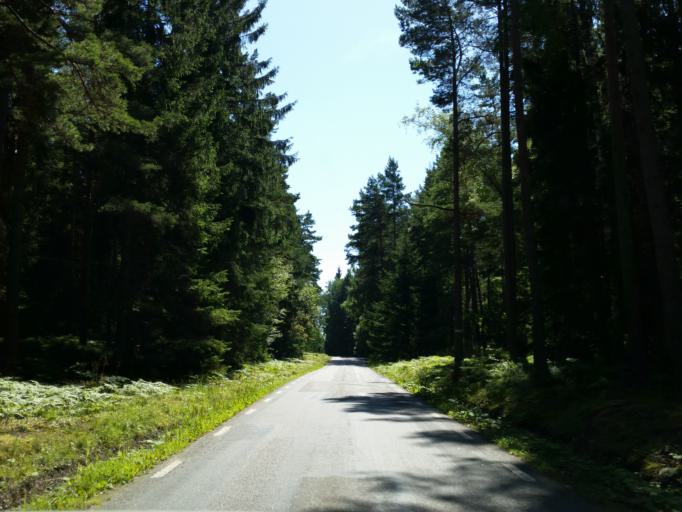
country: SE
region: Soedermanland
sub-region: Trosa Kommun
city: Trosa
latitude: 58.9663
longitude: 17.6570
